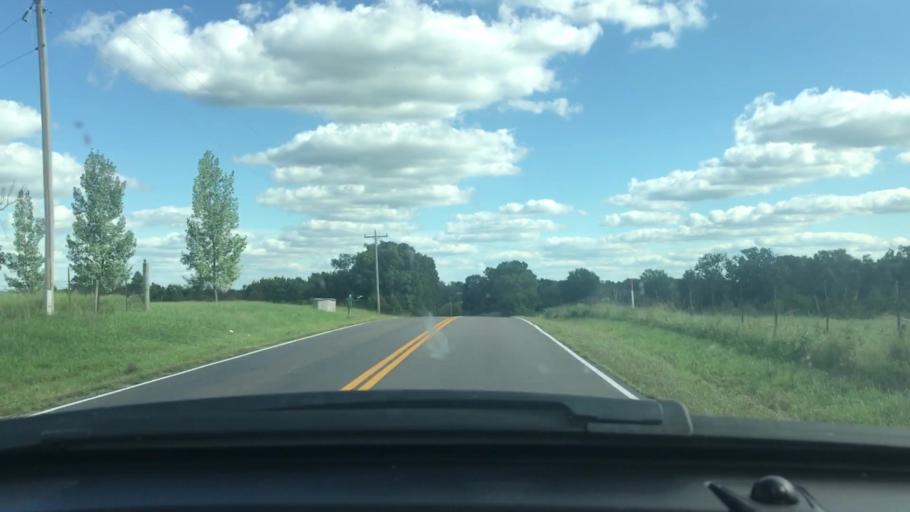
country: US
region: Missouri
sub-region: Wright County
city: Mountain Grove
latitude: 37.3081
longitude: -92.3148
